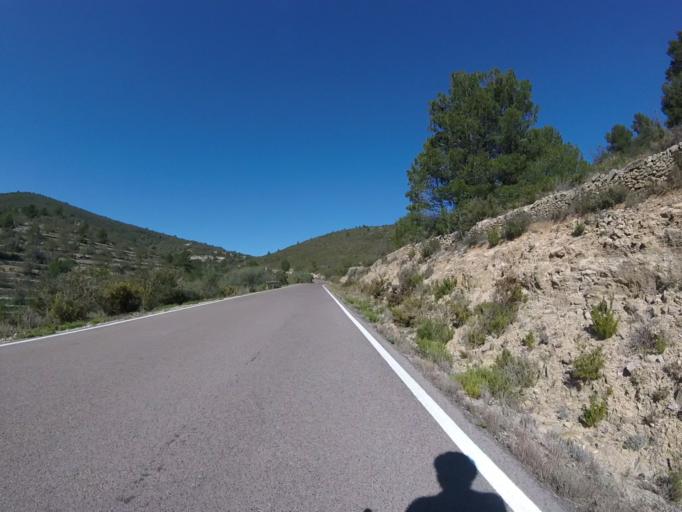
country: ES
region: Valencia
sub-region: Provincia de Castello
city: Santa Magdalena de Pulpis
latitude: 40.3844
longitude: 0.2590
